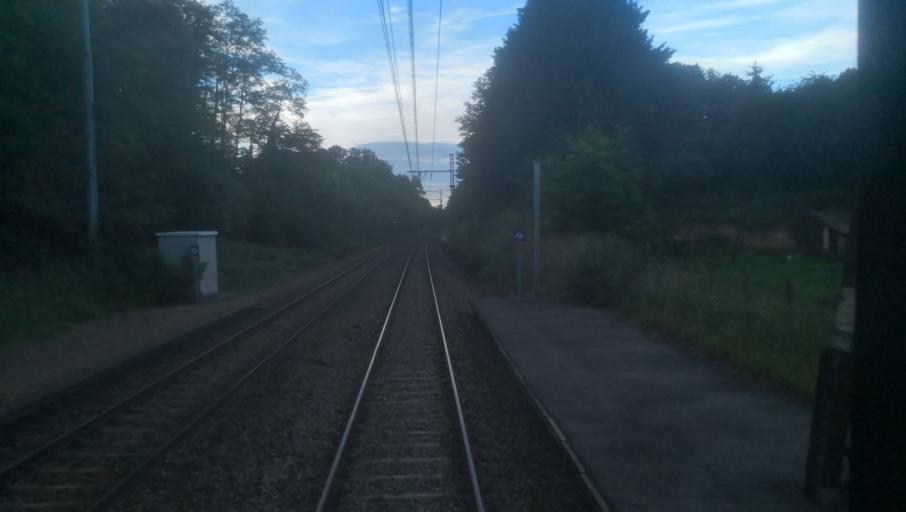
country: FR
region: Limousin
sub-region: Departement de la Creuse
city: Saint-Maurice-la-Souterraine
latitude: 46.1718
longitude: 1.4330
